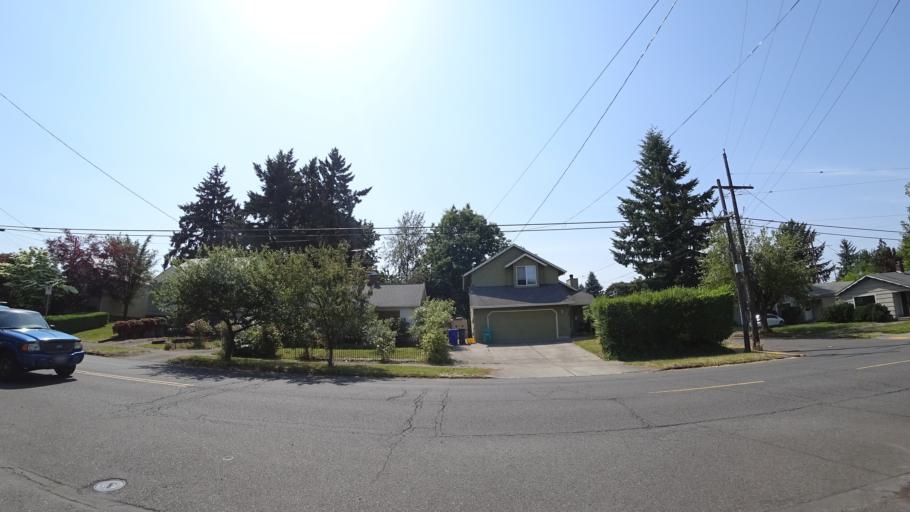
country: US
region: Oregon
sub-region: Multnomah County
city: Portland
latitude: 45.5831
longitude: -122.6971
